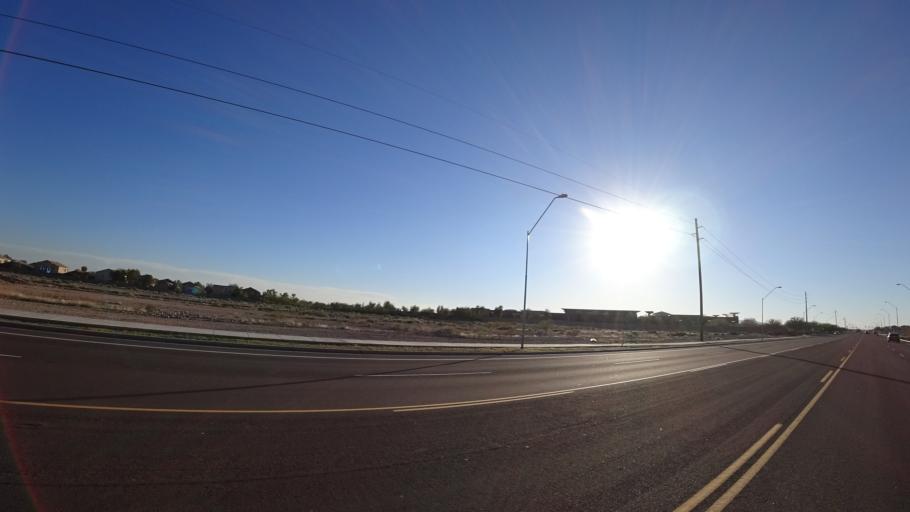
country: US
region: Arizona
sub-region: Maricopa County
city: Sun City West
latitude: 33.6817
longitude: -112.2736
